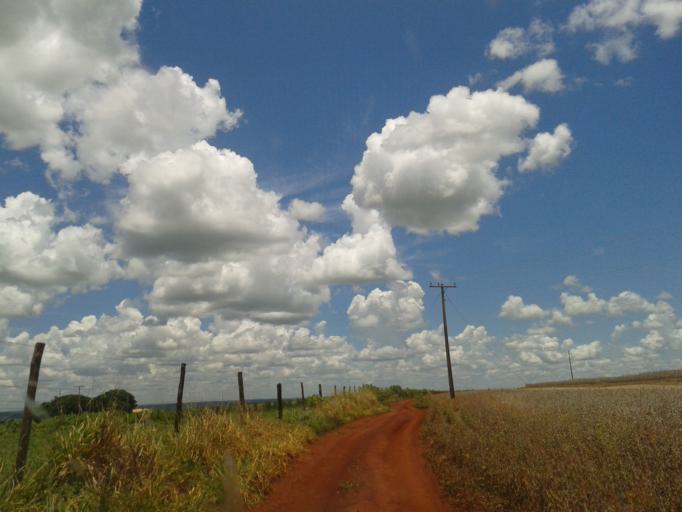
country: BR
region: Minas Gerais
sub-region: Capinopolis
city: Capinopolis
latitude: -18.7618
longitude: -49.7891
